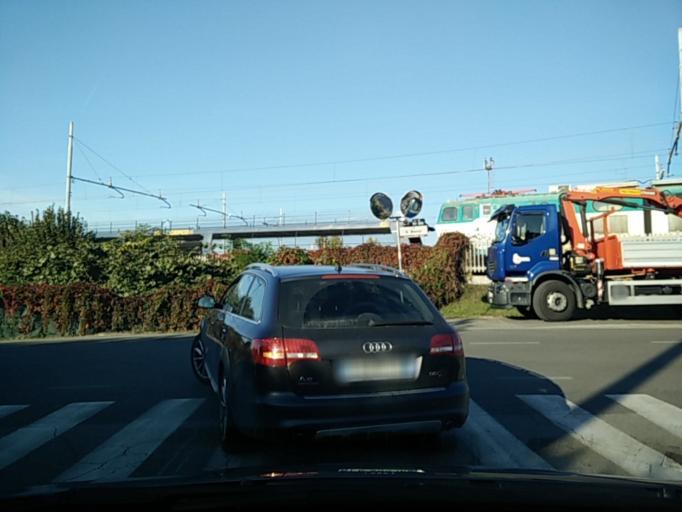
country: IT
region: Veneto
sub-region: Provincia di Treviso
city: Treviso
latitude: 45.6625
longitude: 12.2279
